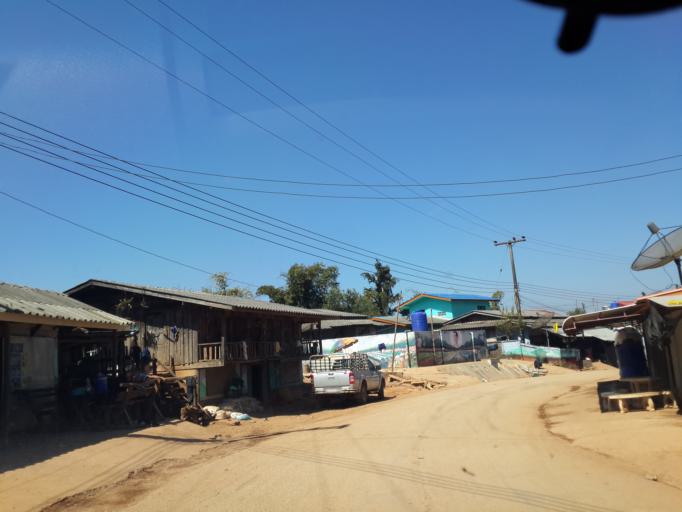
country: TH
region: Chiang Mai
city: Fang
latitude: 19.9366
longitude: 99.0412
